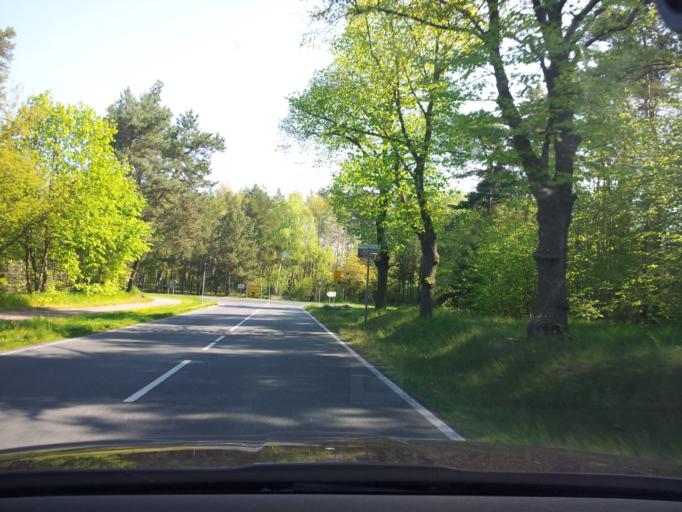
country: DE
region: Brandenburg
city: Juterbog
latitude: 52.0109
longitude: 13.0681
